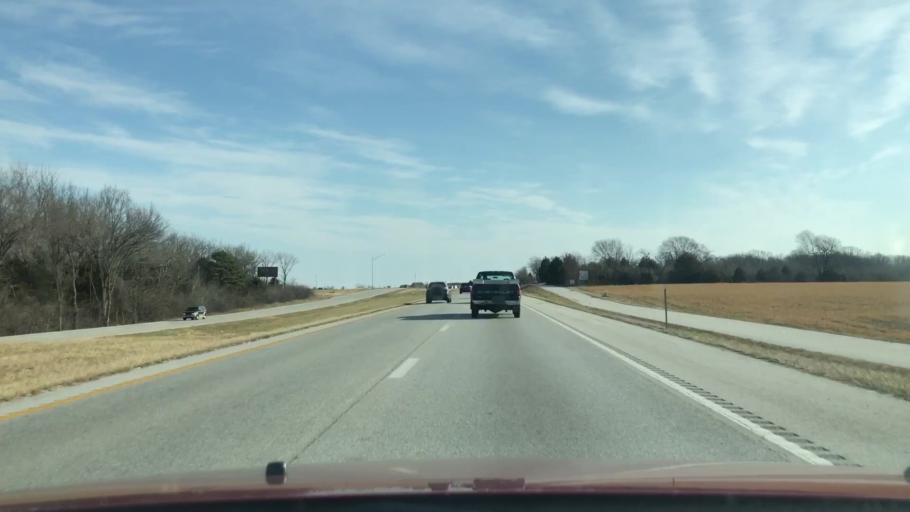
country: US
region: Missouri
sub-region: Webster County
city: Rogersville
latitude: 37.1181
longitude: -93.0991
